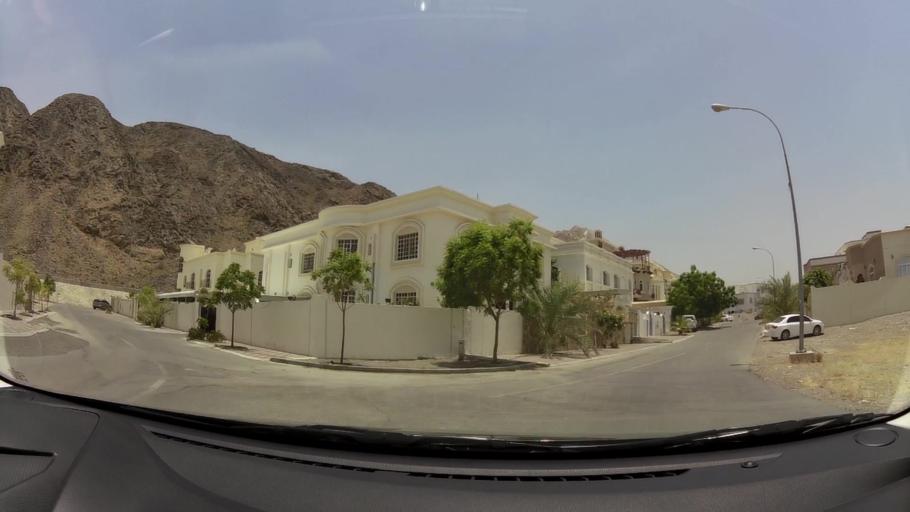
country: OM
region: Muhafazat Masqat
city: Bawshar
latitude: 23.5703
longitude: 58.4294
